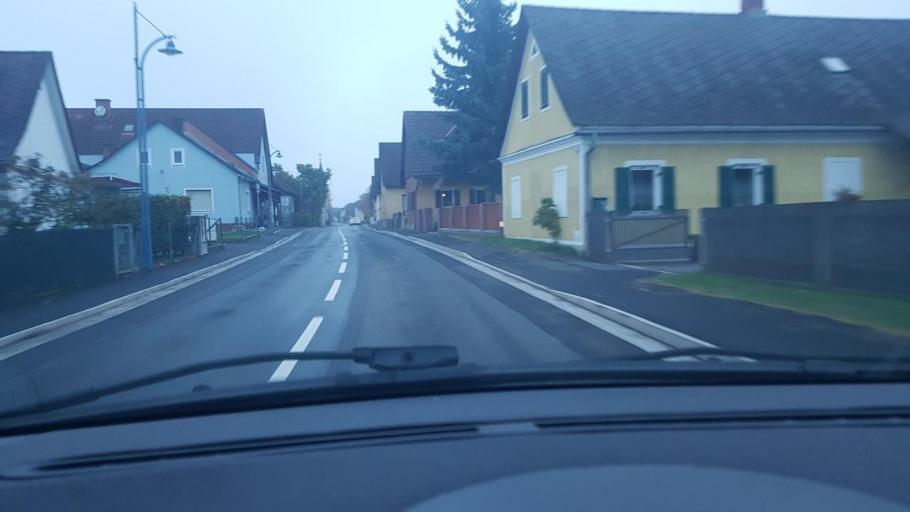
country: AT
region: Styria
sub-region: Politischer Bezirk Leibnitz
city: Obervogau
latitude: 46.7459
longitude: 15.5837
